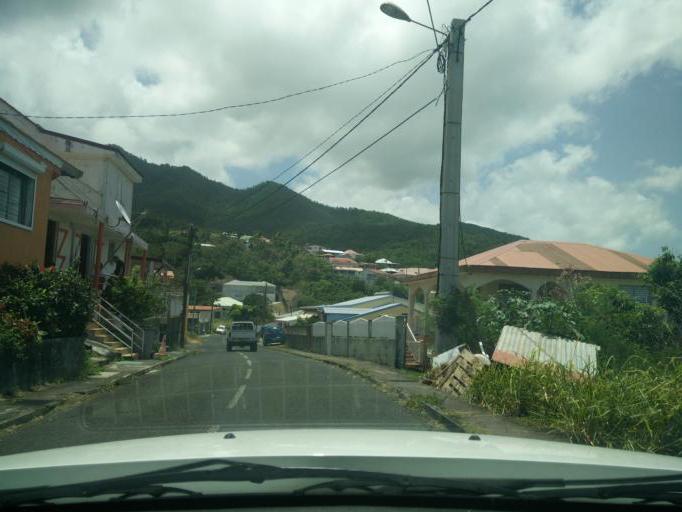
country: GP
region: Guadeloupe
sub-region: Guadeloupe
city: Gourbeyre
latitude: 15.9486
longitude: -61.6961
